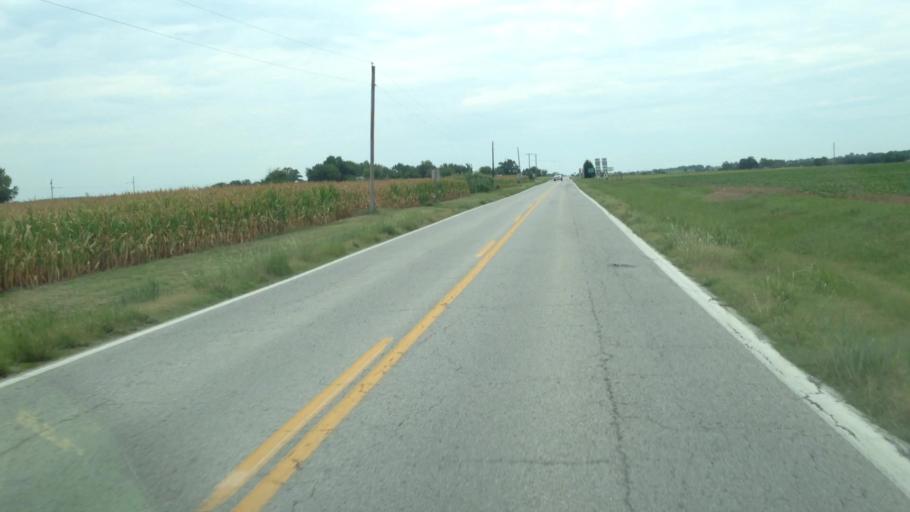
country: US
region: Oklahoma
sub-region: Delaware County
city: Cleora
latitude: 36.6236
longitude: -94.9815
